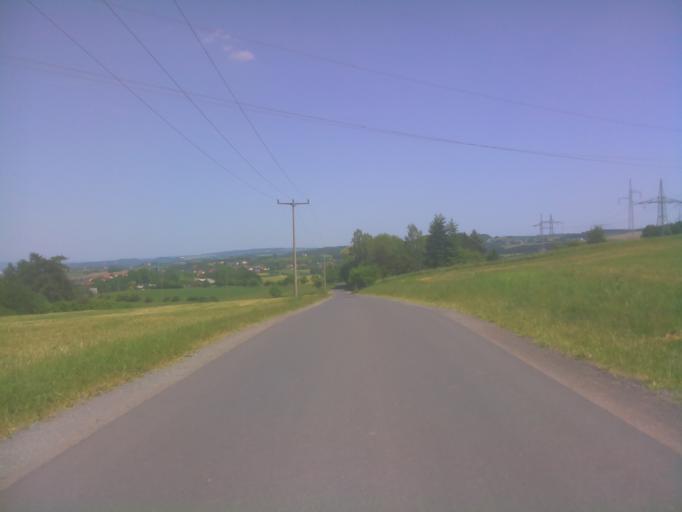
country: DE
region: Thuringia
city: Kaulsdorf
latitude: 50.6392
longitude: 11.4318
